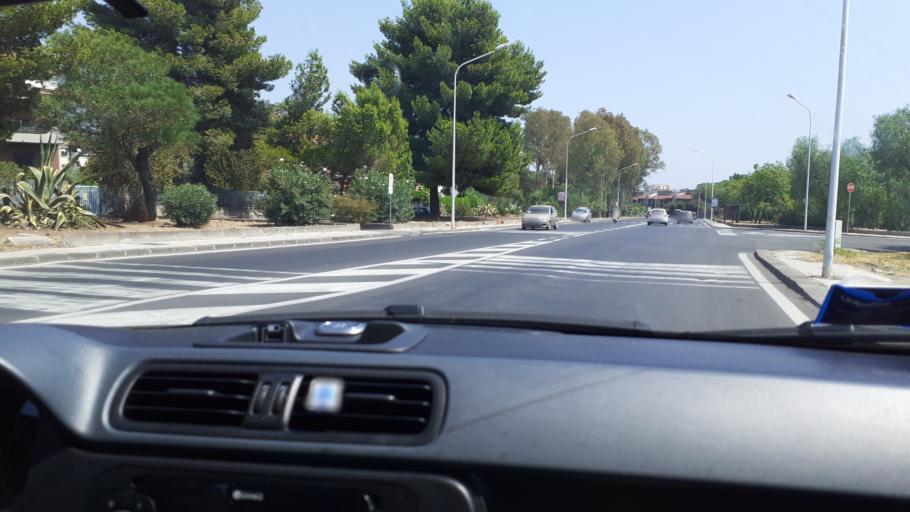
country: IT
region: Sicily
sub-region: Catania
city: Misterbianco
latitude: 37.5155
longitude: 15.0563
